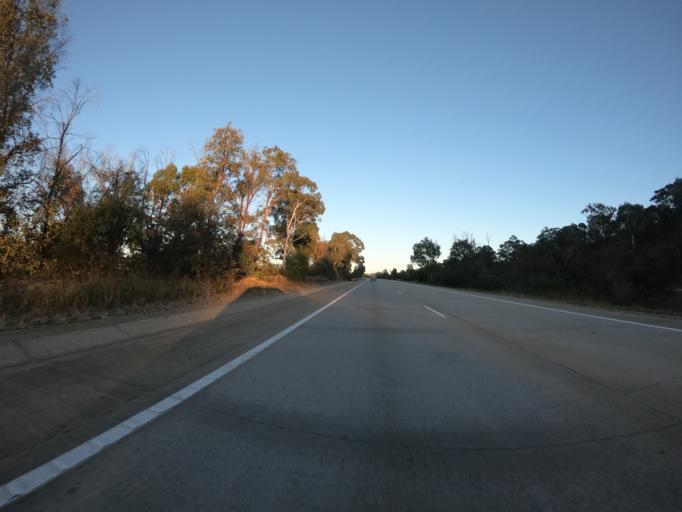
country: AU
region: New South Wales
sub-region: Goulburn Mulwaree
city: Goulburn
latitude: -34.7760
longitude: 149.6967
